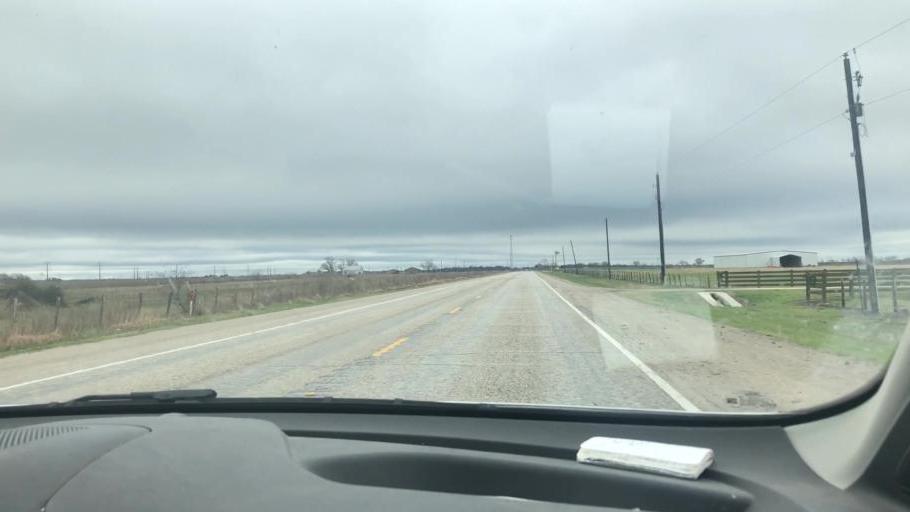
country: US
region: Texas
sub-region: Wharton County
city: Wharton
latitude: 29.2434
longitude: -96.0437
